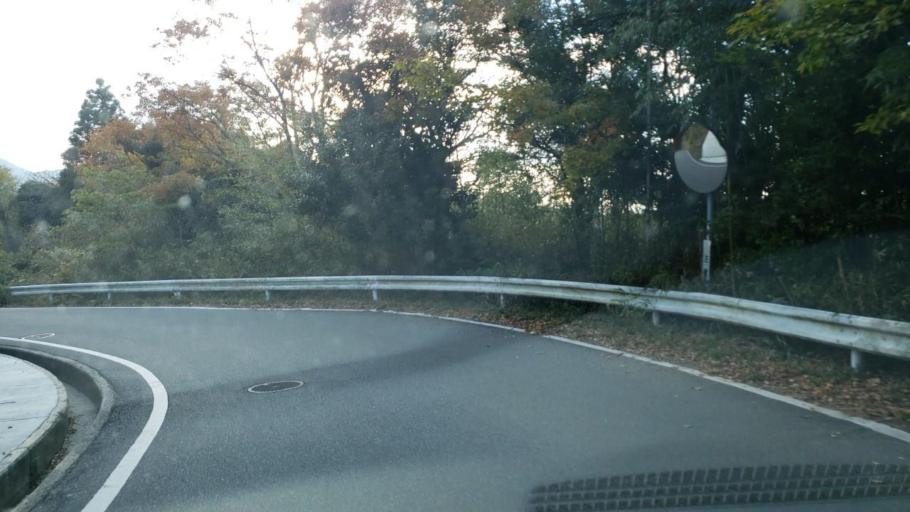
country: JP
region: Hyogo
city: Akashi
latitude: 34.5473
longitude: 134.9727
